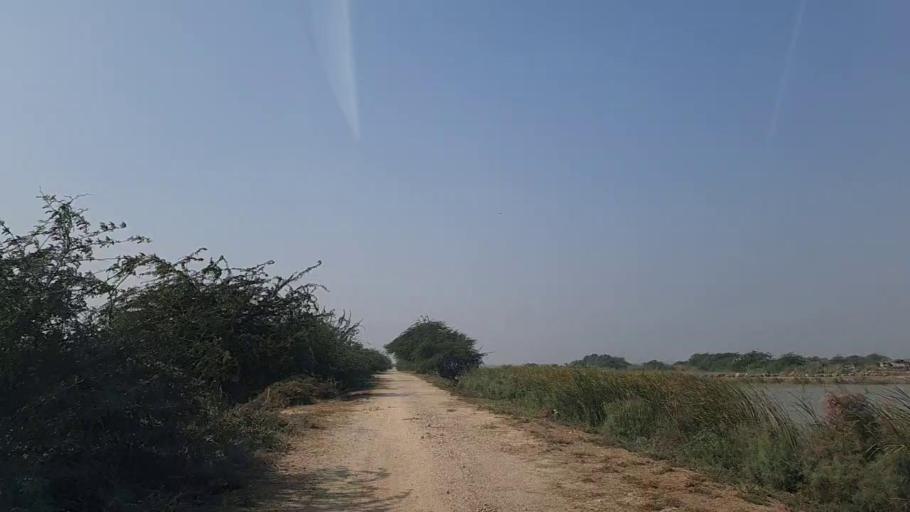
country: PK
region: Sindh
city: Mirpur Sakro
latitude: 24.5749
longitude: 67.7741
